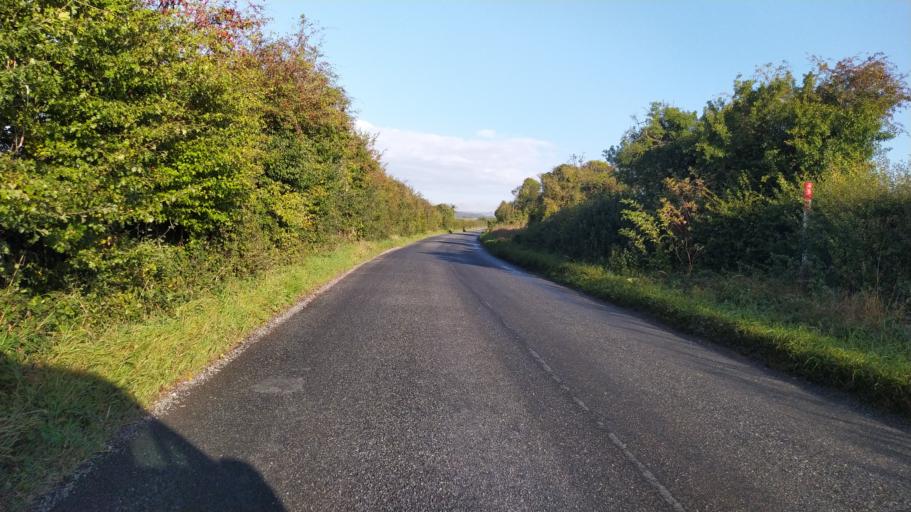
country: GB
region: England
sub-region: Wiltshire
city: Bower Chalke
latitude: 50.9185
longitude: -2.0522
